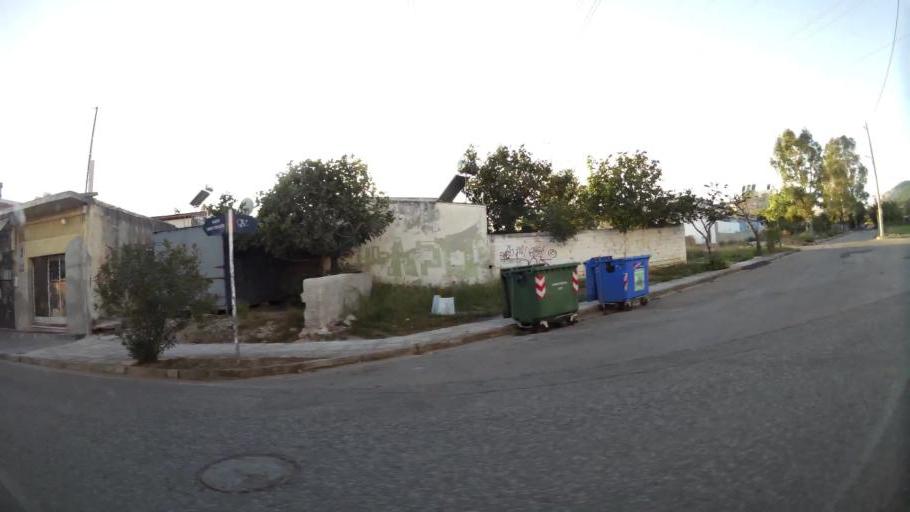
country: GR
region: Attica
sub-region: Nomarchia Dytikis Attikis
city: Ano Liosia
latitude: 38.0906
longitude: 23.7001
